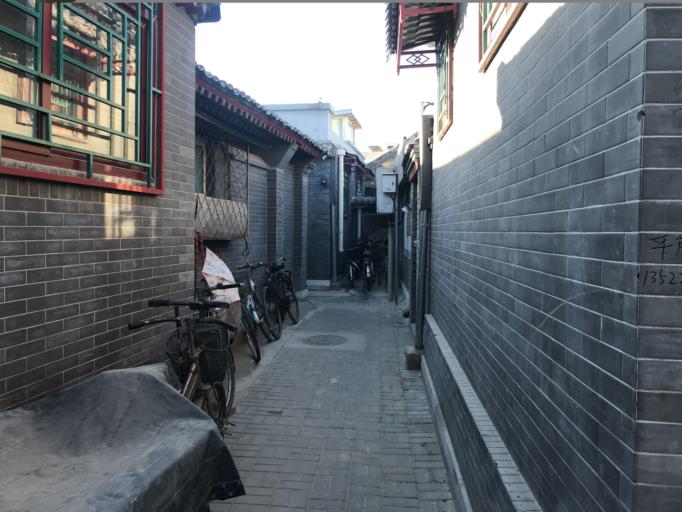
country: CN
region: Beijing
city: Beijing
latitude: 39.8952
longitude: 116.3816
